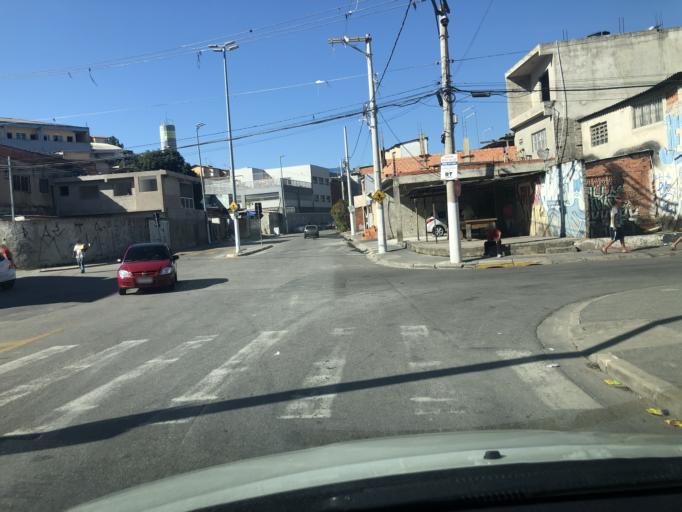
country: BR
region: Sao Paulo
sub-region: Jandira
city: Jandira
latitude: -23.5417
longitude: -46.8916
